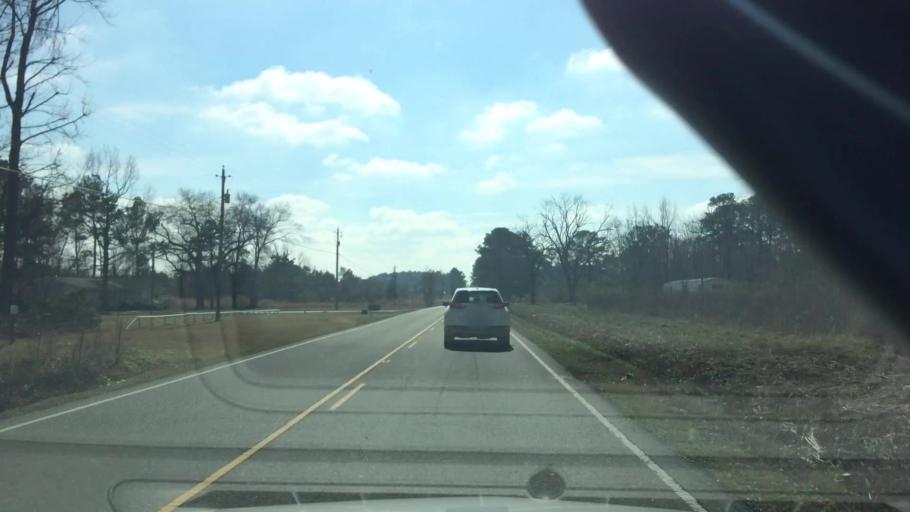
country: US
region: North Carolina
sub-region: Duplin County
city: Beulaville
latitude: 34.8800
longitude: -77.7895
